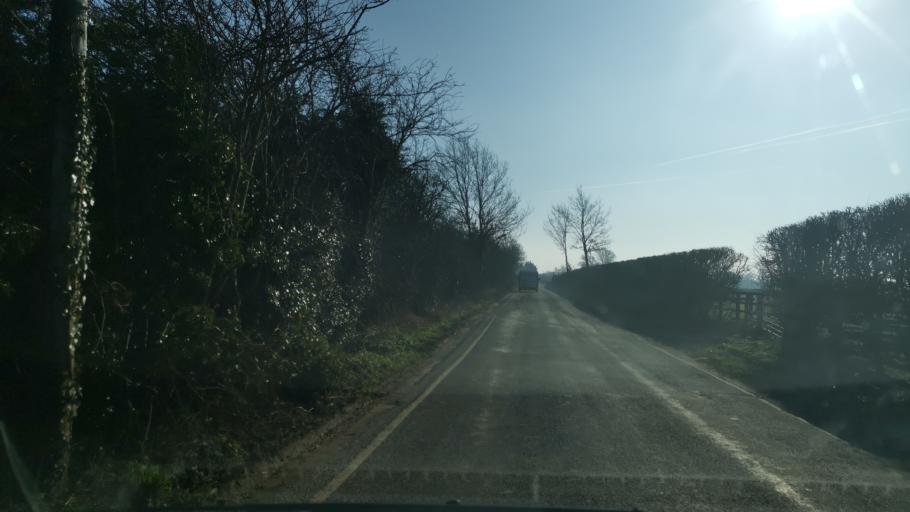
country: GB
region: England
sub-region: City of York
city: Murton
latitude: 53.9744
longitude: -1.0146
